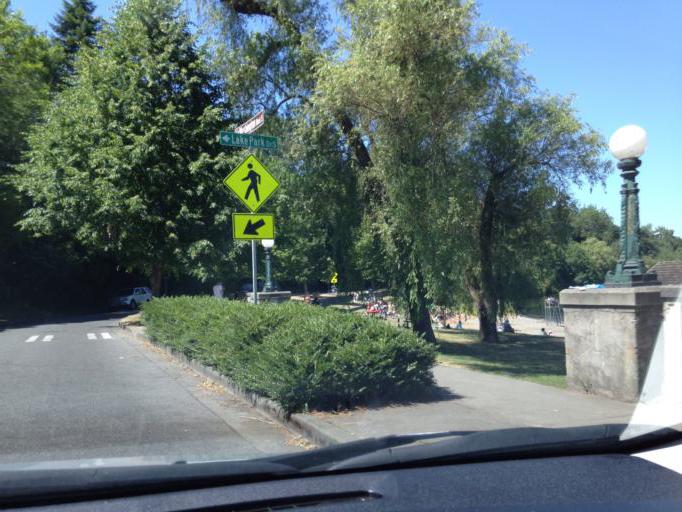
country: US
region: Washington
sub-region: King County
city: Seattle
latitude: 47.5828
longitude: -122.2876
